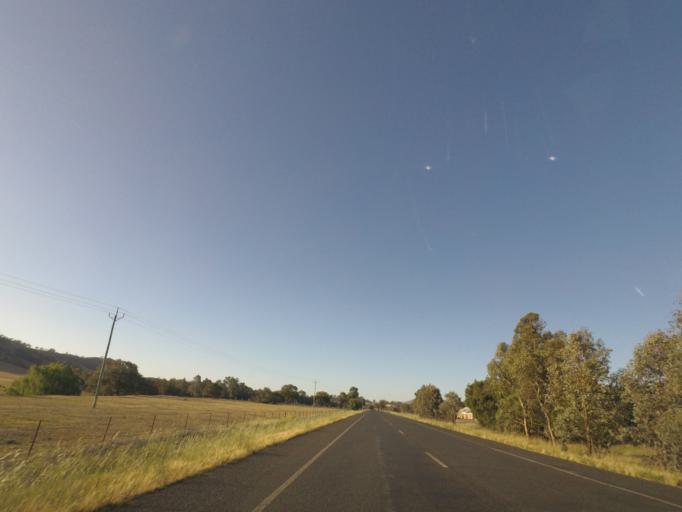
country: AU
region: New South Wales
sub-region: Gundagai
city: Gundagai
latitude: -34.9350
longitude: 148.1671
